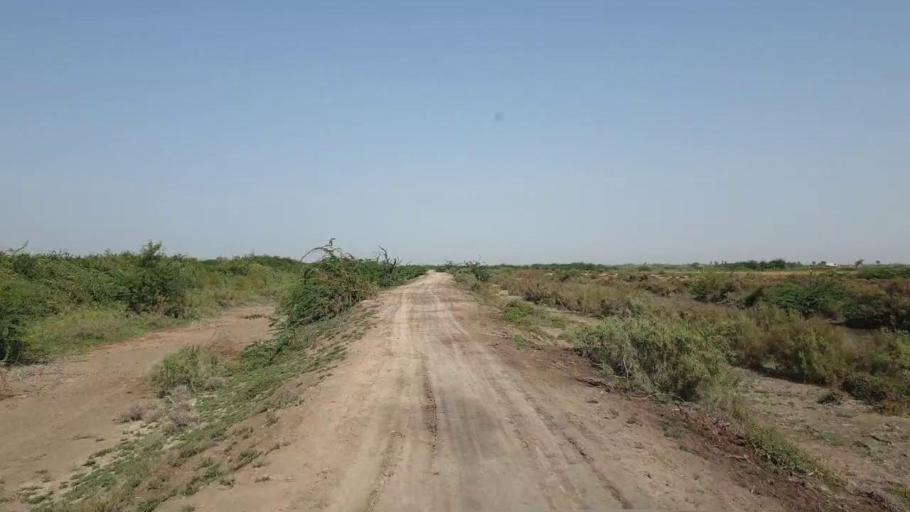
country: PK
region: Sindh
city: Tando Bago
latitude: 24.6535
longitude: 69.0706
